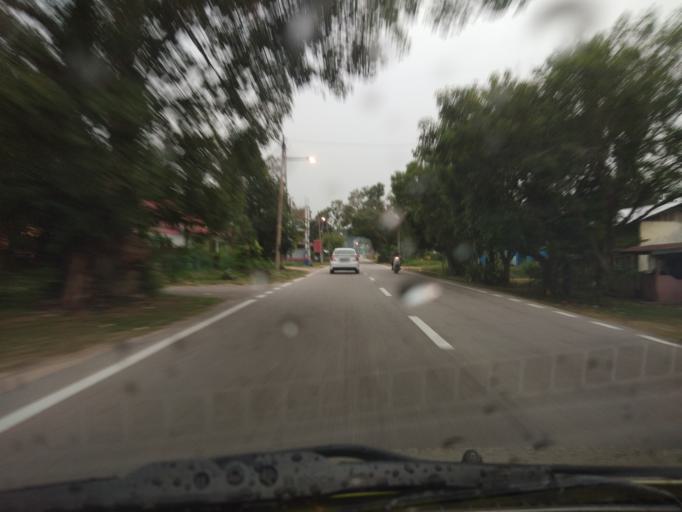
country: MY
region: Penang
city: Permatang Kuching
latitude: 5.4818
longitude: 100.4012
